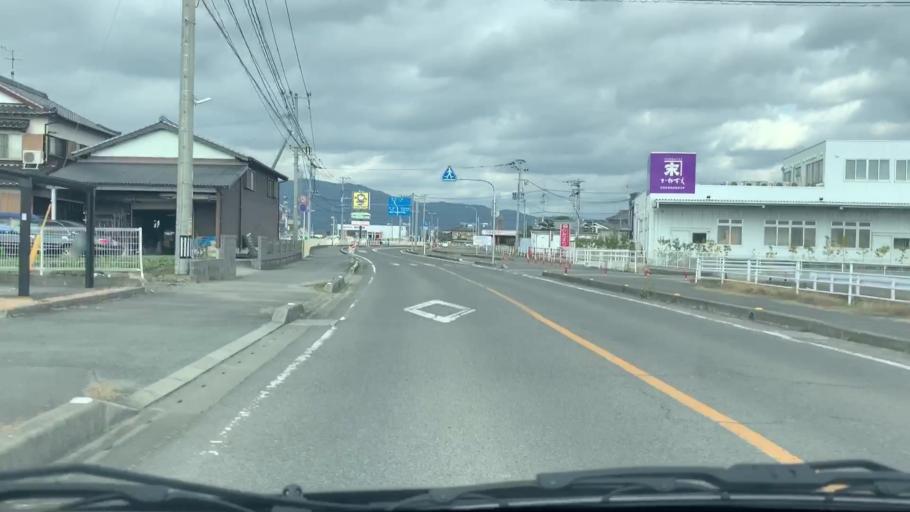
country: JP
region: Saga Prefecture
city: Saga-shi
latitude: 33.2479
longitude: 130.2376
